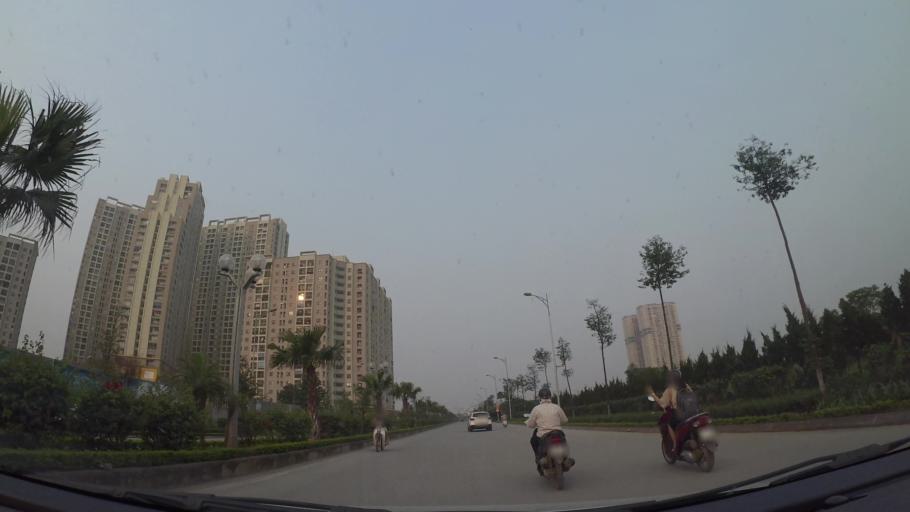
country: VN
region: Ha Noi
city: Cau Dien
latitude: 21.0041
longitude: 105.7265
